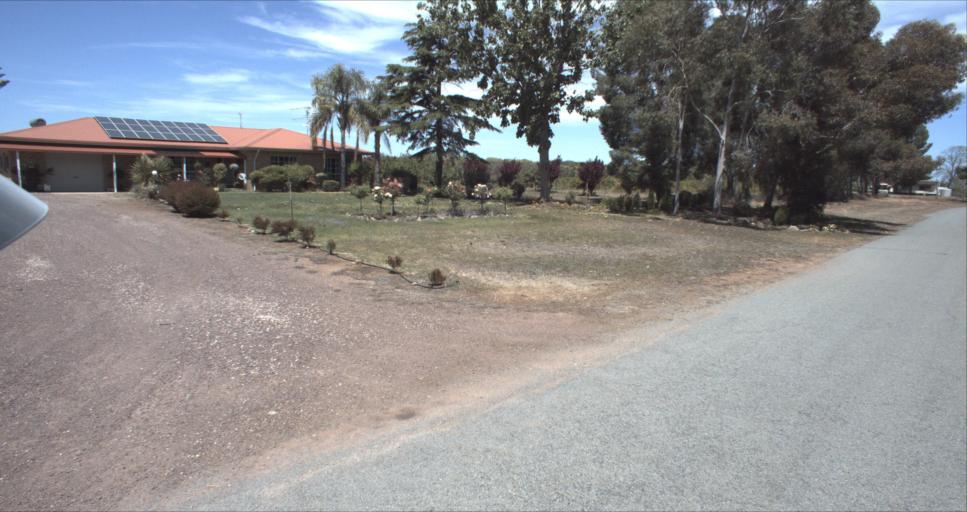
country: AU
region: New South Wales
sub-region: Narrandera
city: Narrandera
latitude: -34.6766
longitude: 146.4416
